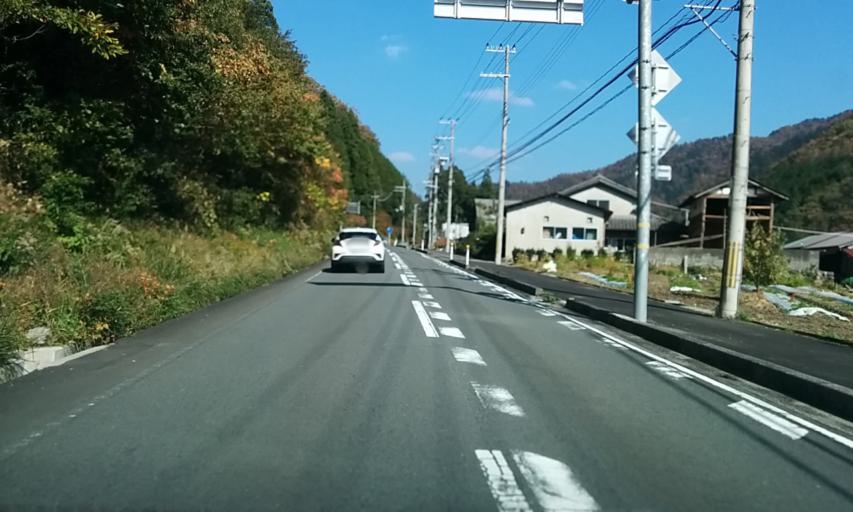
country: JP
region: Fukui
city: Obama
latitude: 35.2819
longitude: 135.5923
